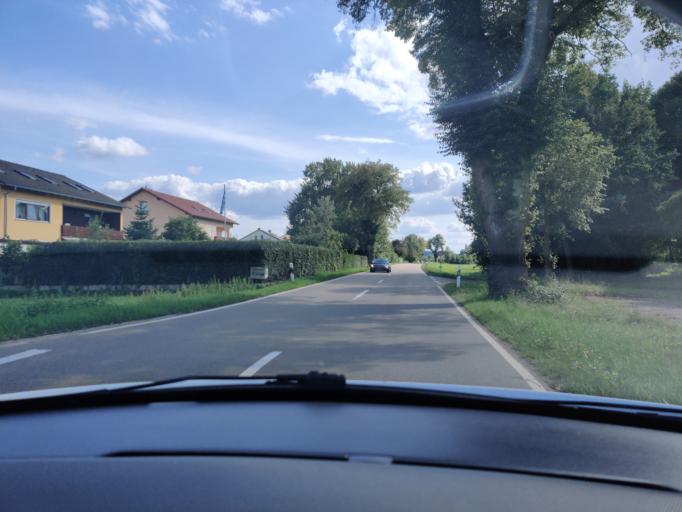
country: DE
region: Bavaria
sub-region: Upper Palatinate
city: Nabburg
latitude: 49.4627
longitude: 12.1860
